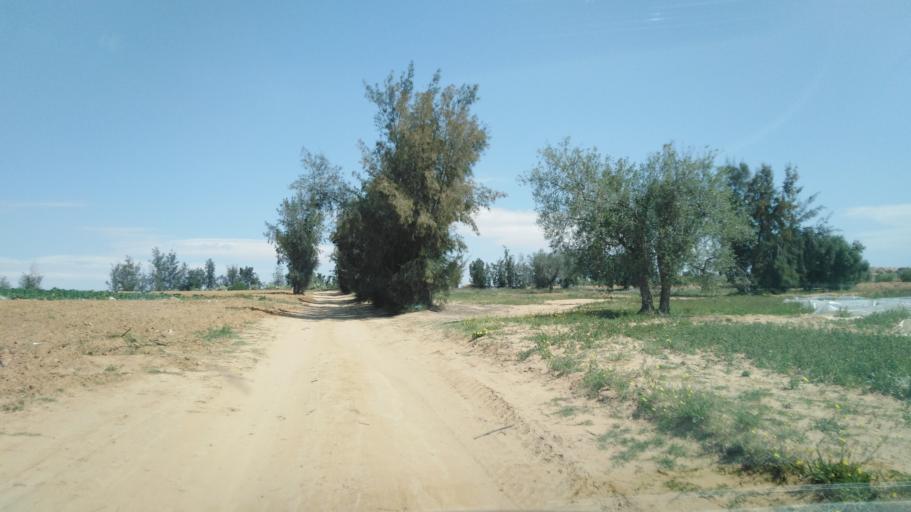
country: TN
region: Safaqis
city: Sfax
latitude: 34.7705
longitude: 10.5278
